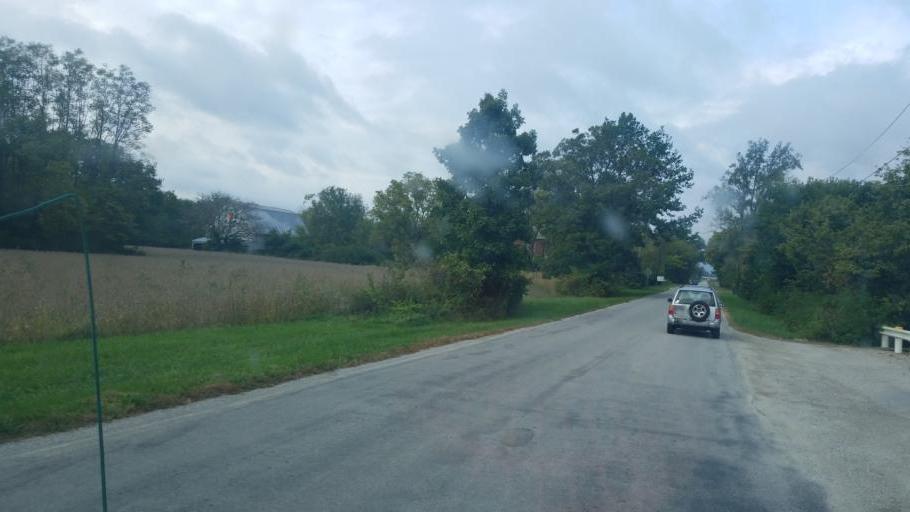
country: US
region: Ohio
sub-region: Wood County
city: North Baltimore
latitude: 41.1822
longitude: -83.6313
